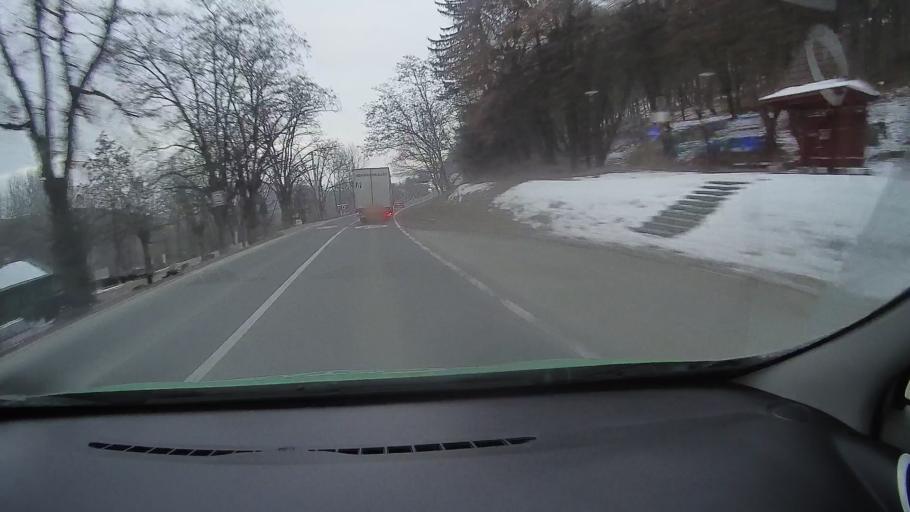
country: RO
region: Harghita
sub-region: Municipiul Odorheiu Secuiesc
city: Odorheiu Secuiesc
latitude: 46.3310
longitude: 25.2742
